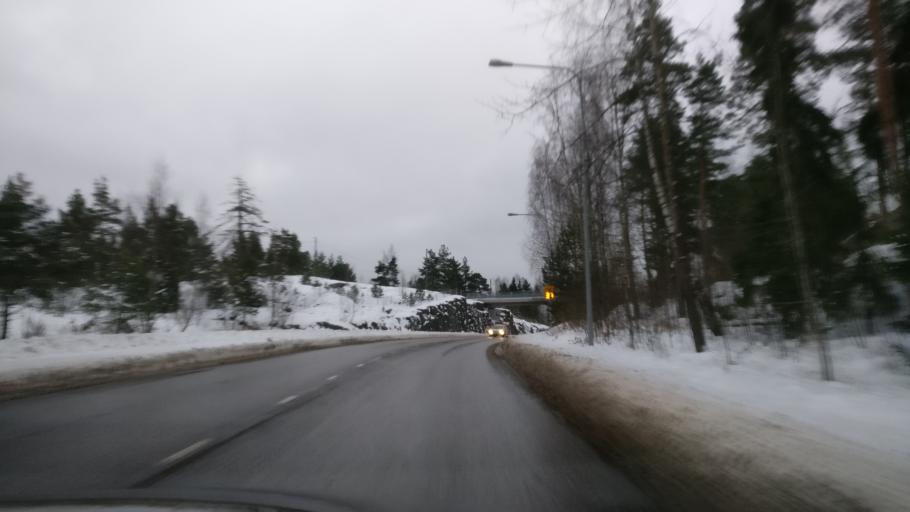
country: FI
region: Uusimaa
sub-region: Helsinki
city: Helsinki
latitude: 60.1740
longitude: 25.0497
